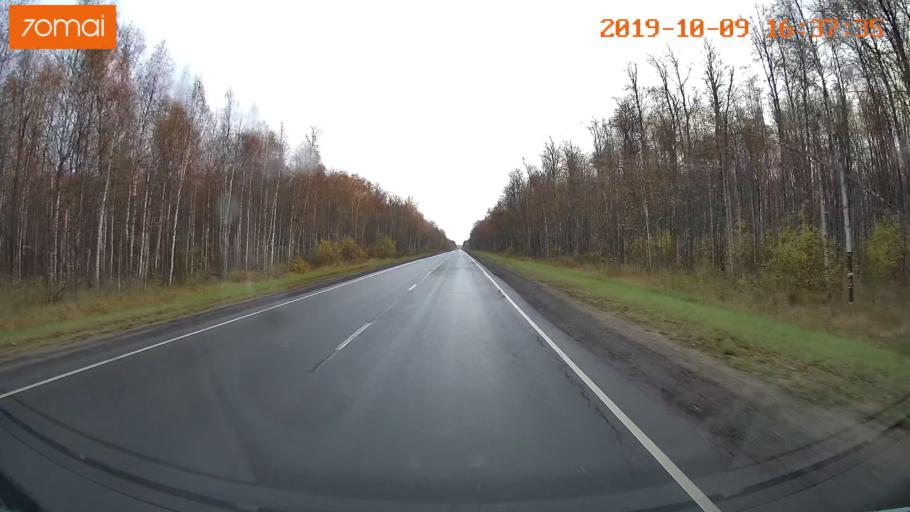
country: RU
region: Kostroma
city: Volgorechensk
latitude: 57.5247
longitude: 41.0265
